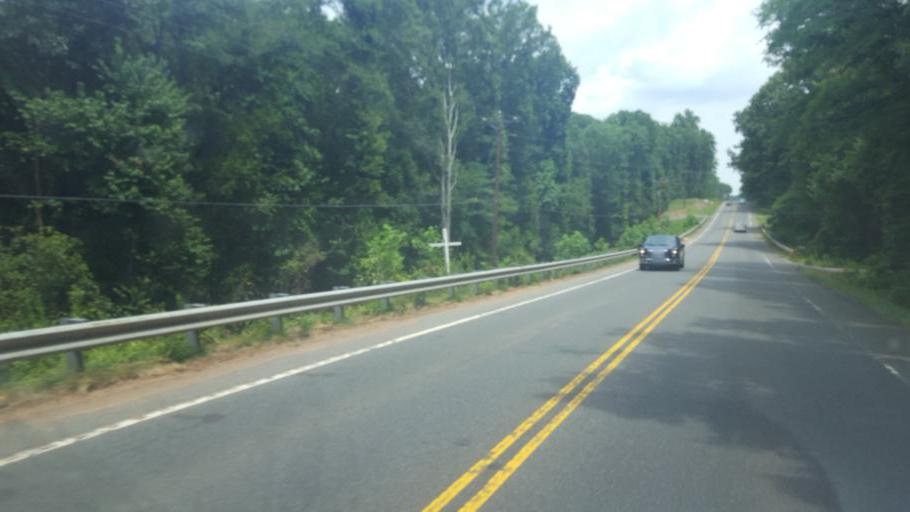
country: US
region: South Carolina
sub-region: York County
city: Newport
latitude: 34.9555
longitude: -81.1240
